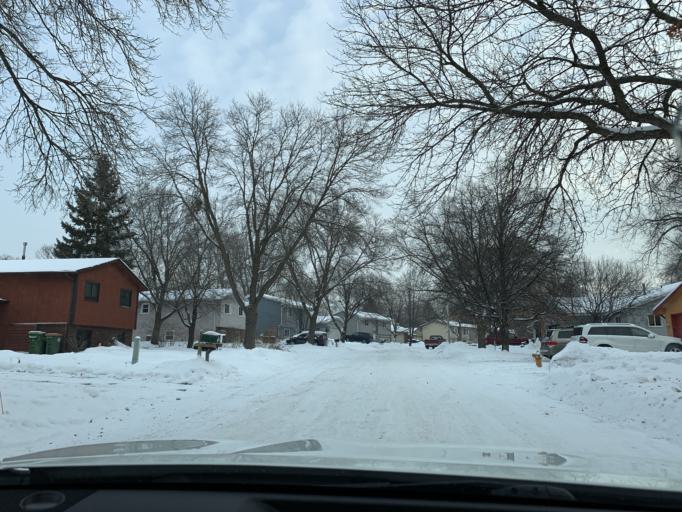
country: US
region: Minnesota
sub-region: Anoka County
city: Coon Rapids
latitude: 45.1592
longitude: -93.2926
